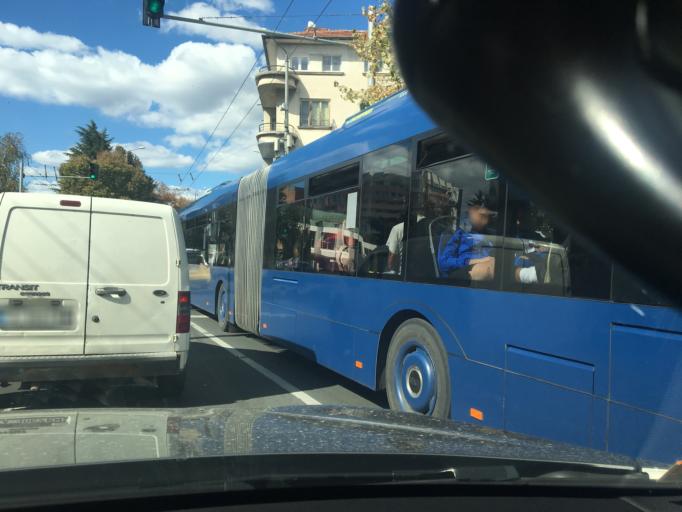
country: BG
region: Burgas
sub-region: Obshtina Burgas
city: Burgas
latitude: 42.4931
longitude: 27.4709
